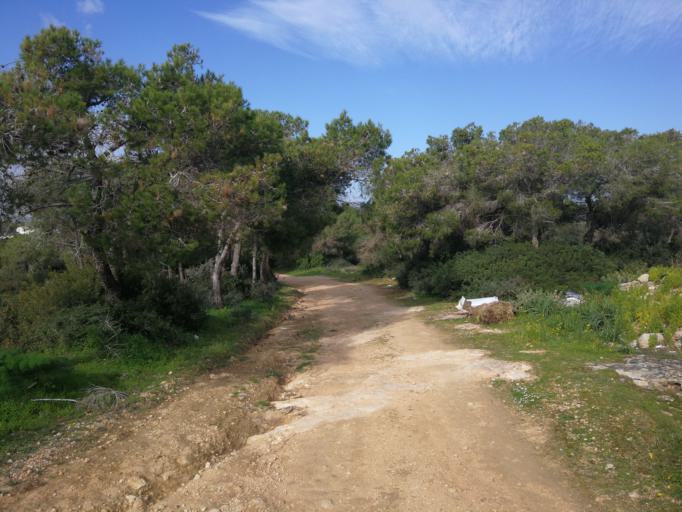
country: TN
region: Tunis
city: Al Marsa
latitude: 36.9018
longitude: 10.2973
